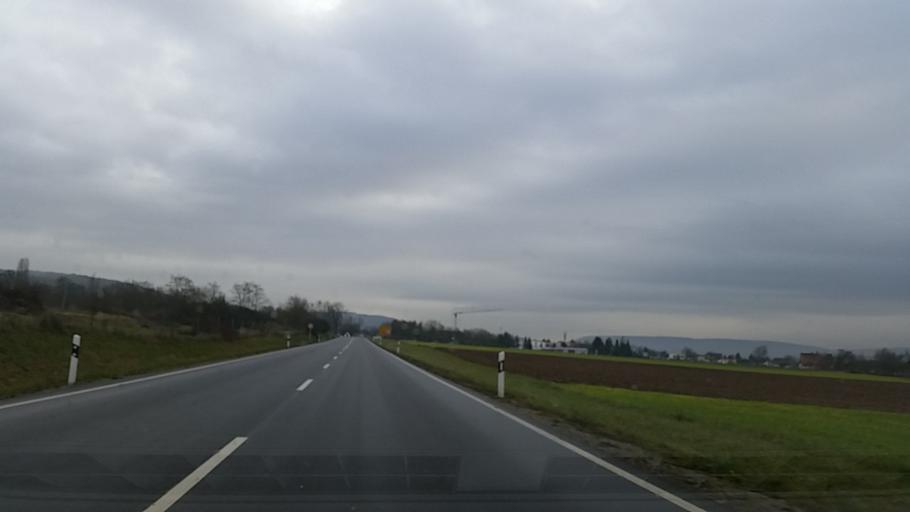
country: DE
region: Bavaria
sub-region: Regierungsbezirk Unterfranken
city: Himmelstadt
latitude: 49.9276
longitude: 9.8108
